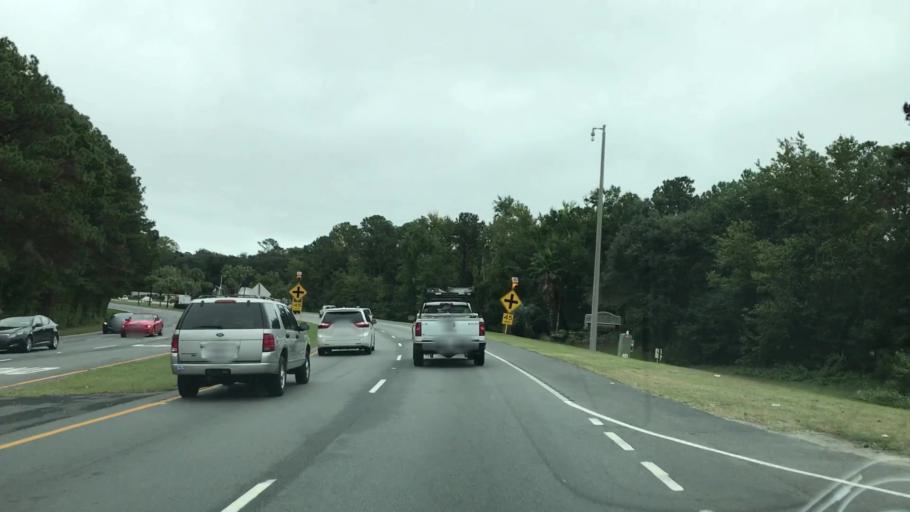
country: US
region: South Carolina
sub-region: Beaufort County
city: Hilton Head Island
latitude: 32.2190
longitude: -80.7765
